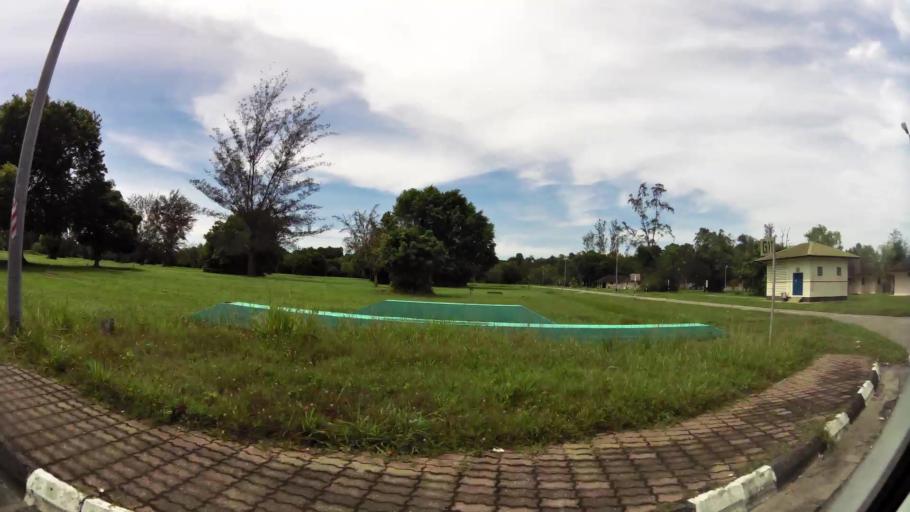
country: BN
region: Belait
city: Seria
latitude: 4.6033
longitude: 114.2934
